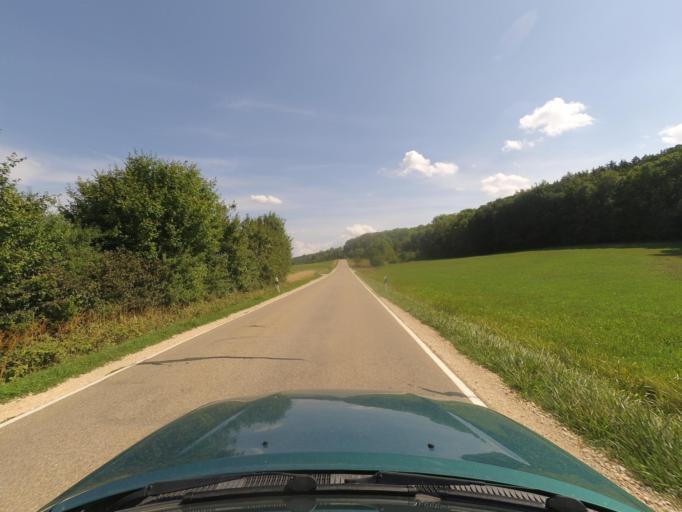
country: DE
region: Bavaria
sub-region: Regierungsbezirk Mittelfranken
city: Ettenstatt
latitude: 49.0755
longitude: 11.0691
